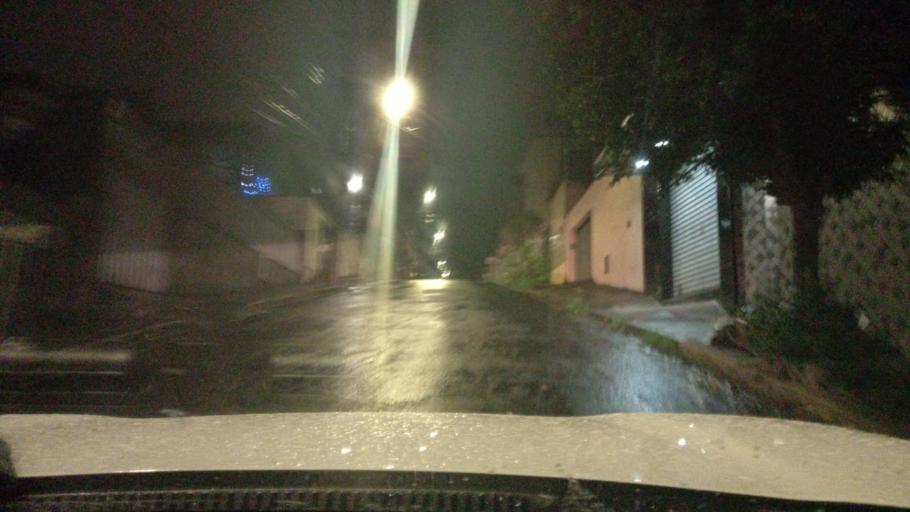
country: BR
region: Minas Gerais
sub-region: Belo Horizonte
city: Belo Horizonte
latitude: -19.8991
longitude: -43.9203
